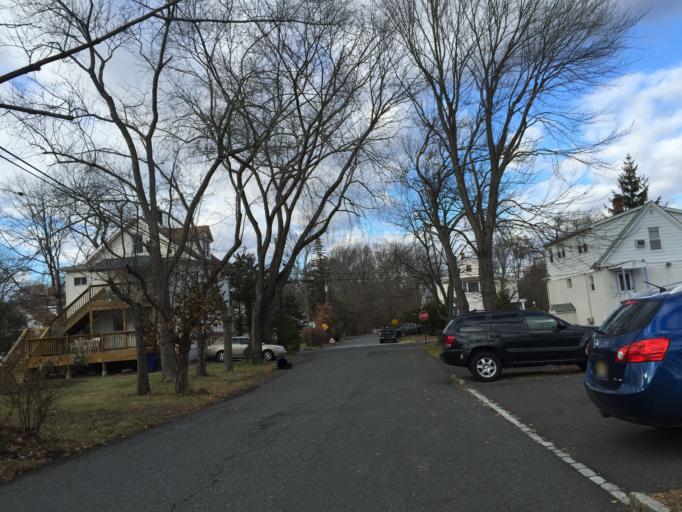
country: US
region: New Jersey
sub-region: Union County
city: New Providence
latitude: 40.7002
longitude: -74.4000
